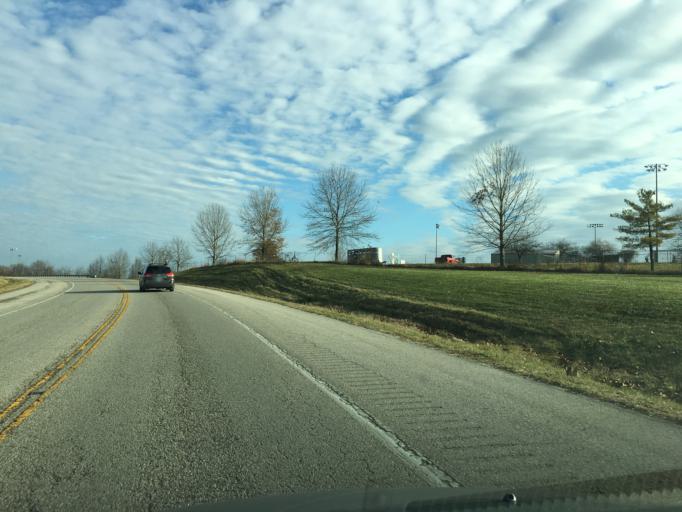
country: US
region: Kentucky
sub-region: Scott County
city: Georgetown
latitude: 38.2388
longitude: -84.5750
